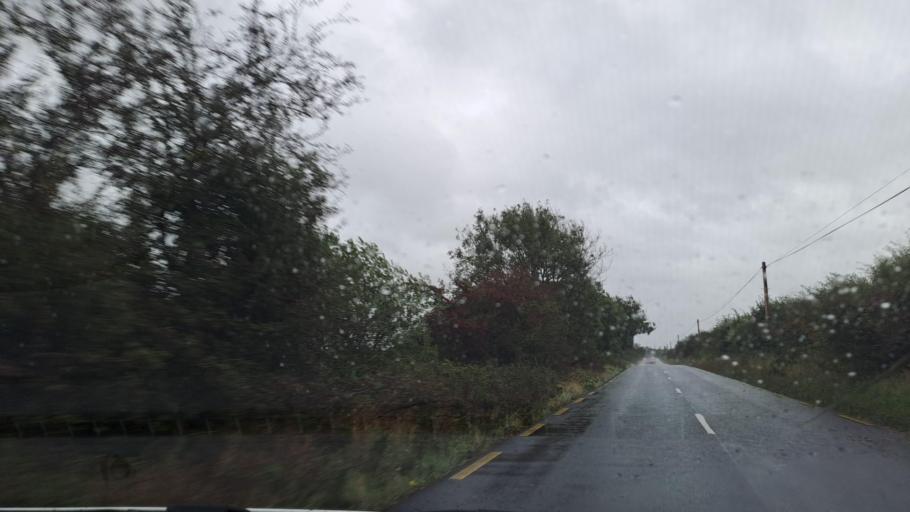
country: GB
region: Northern Ireland
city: Crossmaglen
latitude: 53.9709
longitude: -6.5895
